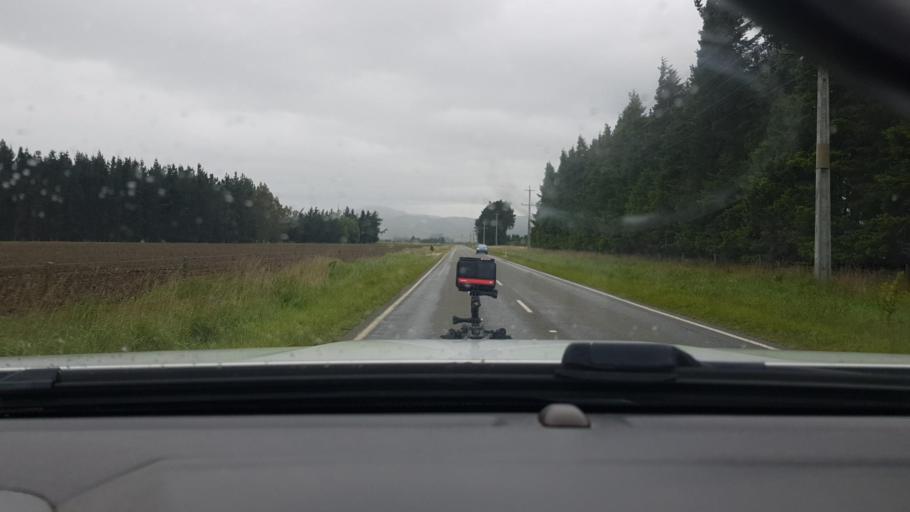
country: NZ
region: Southland
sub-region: Southland District
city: Winton
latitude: -45.7709
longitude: 168.4054
